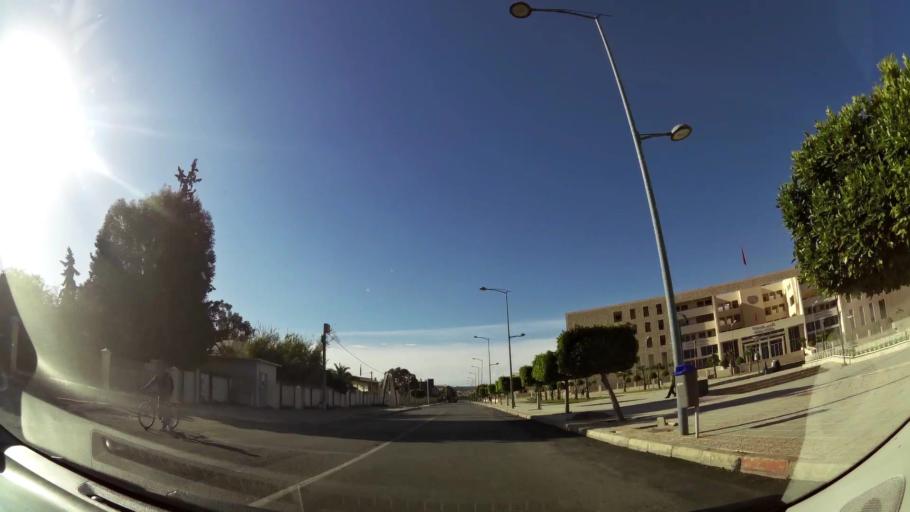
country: MA
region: Oriental
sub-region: Oujda-Angad
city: Oujda
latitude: 34.6612
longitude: -1.9110
